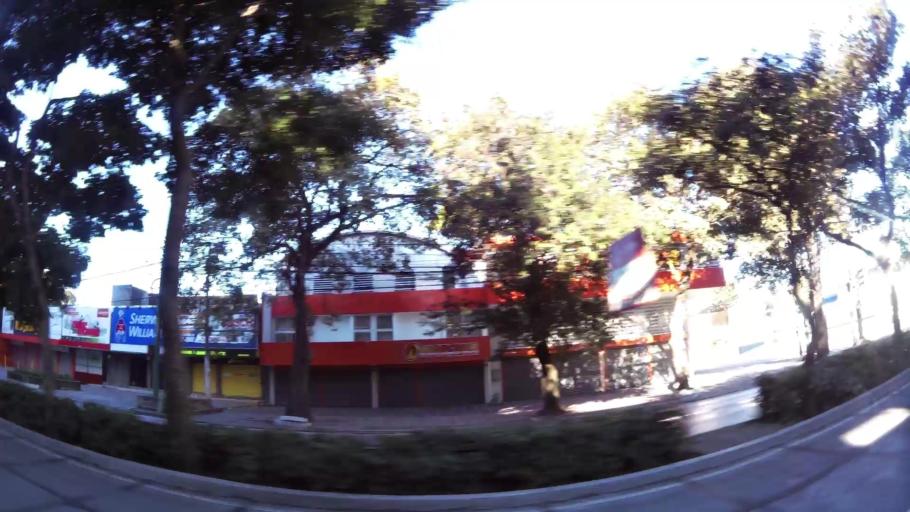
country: GT
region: Guatemala
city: Guatemala City
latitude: 14.6117
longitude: -90.5169
